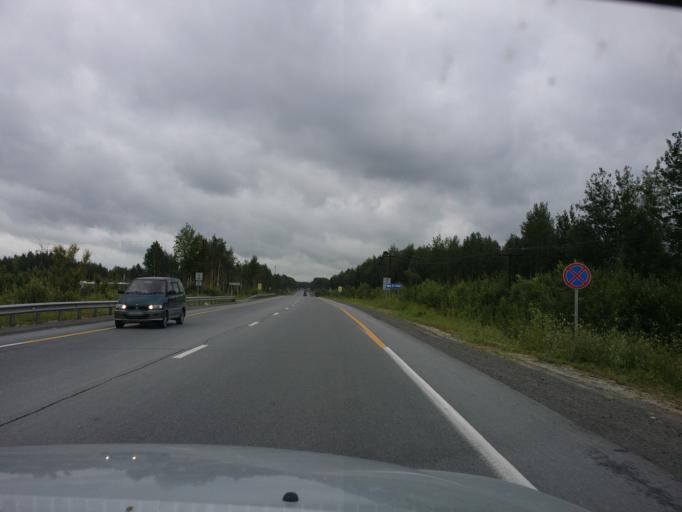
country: RU
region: Khanty-Mansiyskiy Avtonomnyy Okrug
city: Nizhnevartovsk
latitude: 61.0228
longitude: 76.3731
